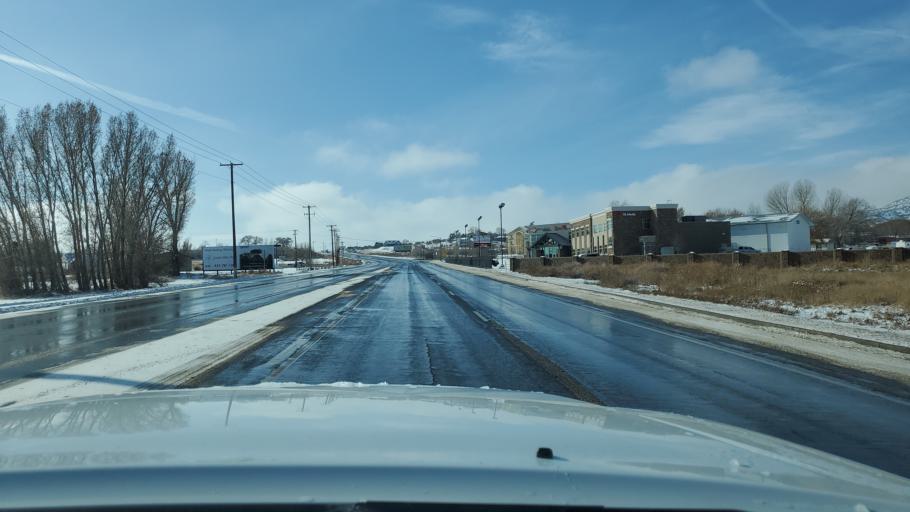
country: US
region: Utah
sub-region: Uintah County
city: Maeser
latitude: 40.4351
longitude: -109.5706
